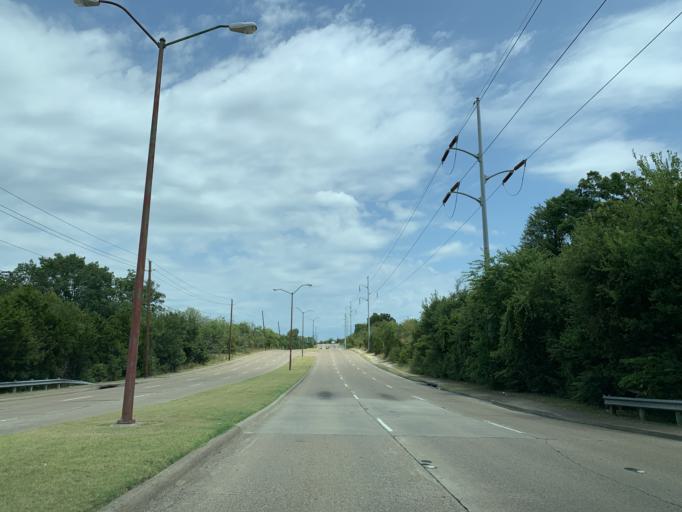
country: US
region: Texas
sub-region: Dallas County
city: DeSoto
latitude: 32.6623
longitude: -96.8105
